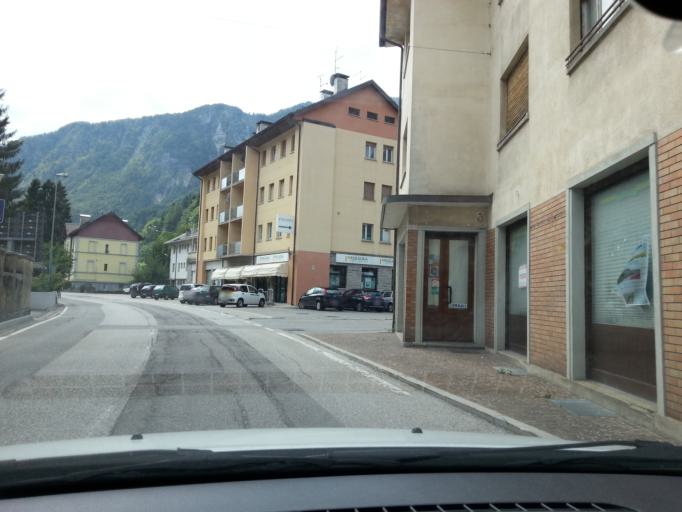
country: IT
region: Friuli Venezia Giulia
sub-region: Provincia di Udine
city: Pontebba
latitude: 46.5053
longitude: 13.3046
